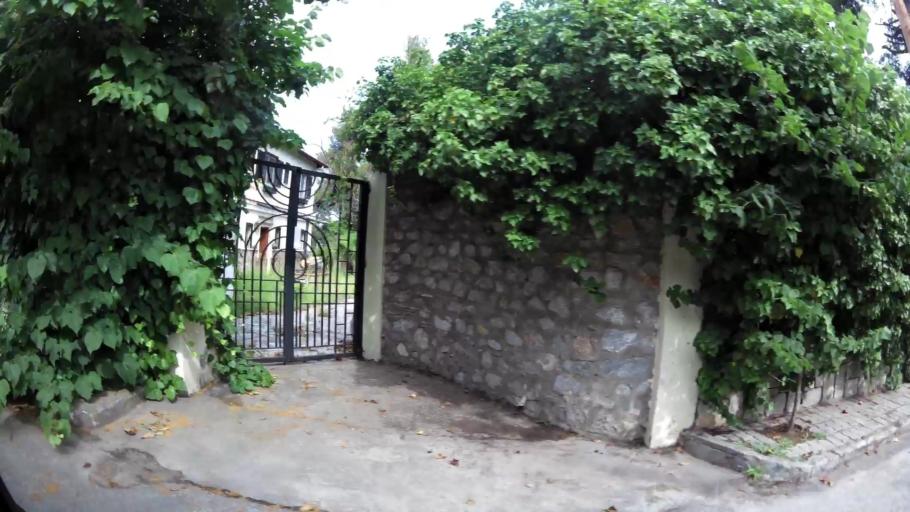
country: GR
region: Central Macedonia
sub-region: Nomos Thessalonikis
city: Panorama
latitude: 40.5935
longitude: 23.0102
